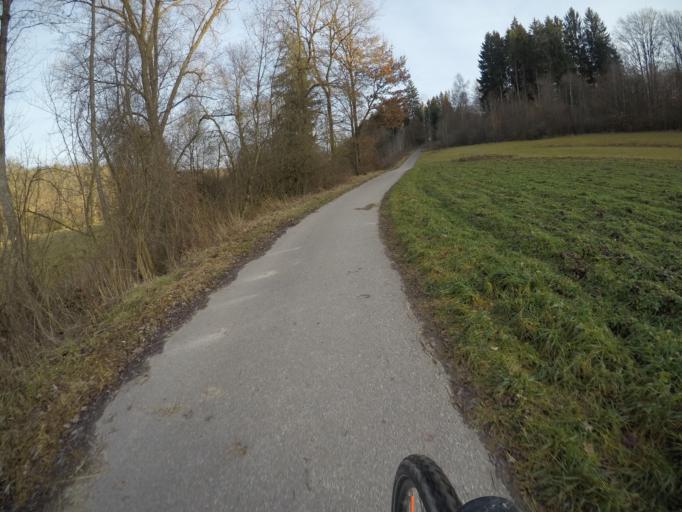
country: DE
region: Baden-Wuerttemberg
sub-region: Regierungsbezirk Stuttgart
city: Steinenbronn
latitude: 48.6509
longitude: 9.0935
